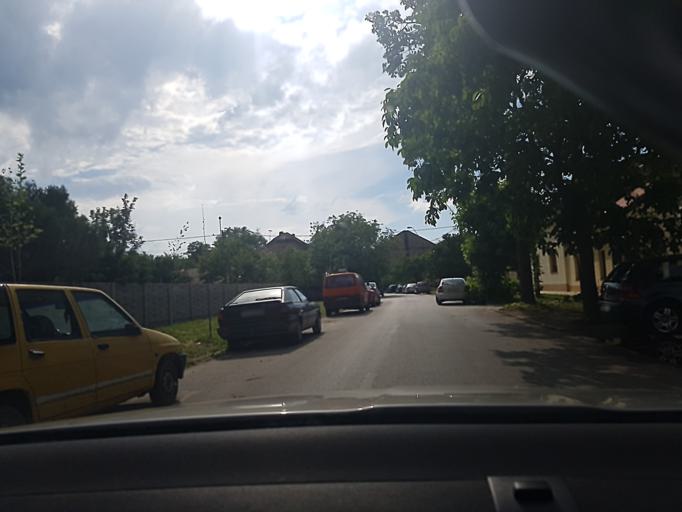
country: RO
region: Timis
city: Timisoara
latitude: 45.7379
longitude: 21.2189
